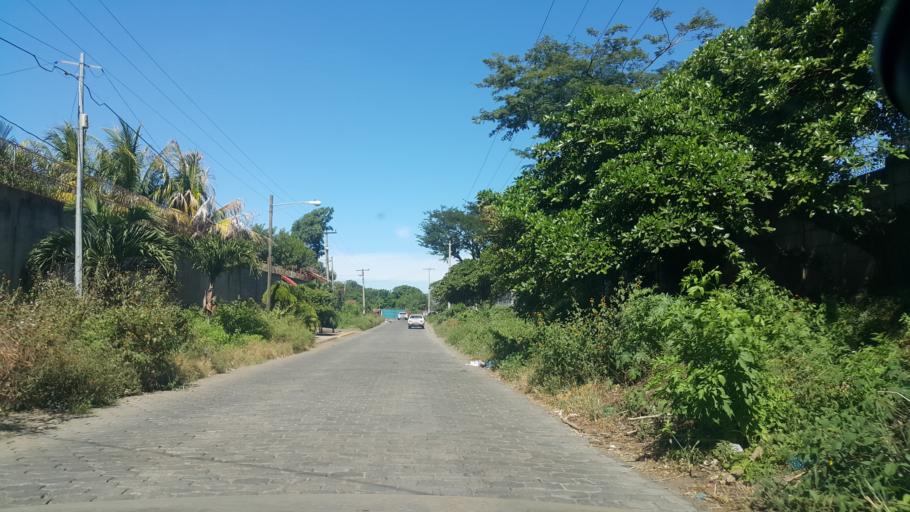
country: NI
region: Managua
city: Ciudad Sandino
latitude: 12.1450
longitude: -86.3373
